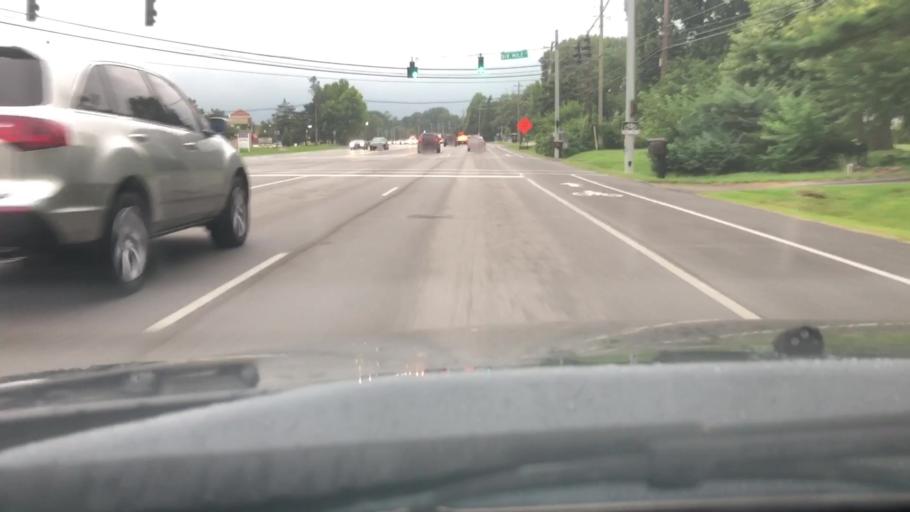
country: US
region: Kentucky
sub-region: Jefferson County
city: Hurstbourne Acres
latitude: 38.2111
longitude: -85.5864
